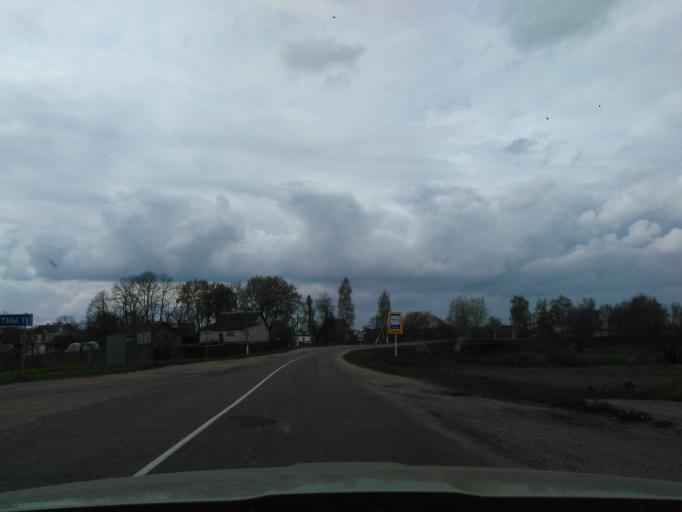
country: BY
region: Vitebsk
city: Chashniki
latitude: 54.8410
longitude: 29.1831
